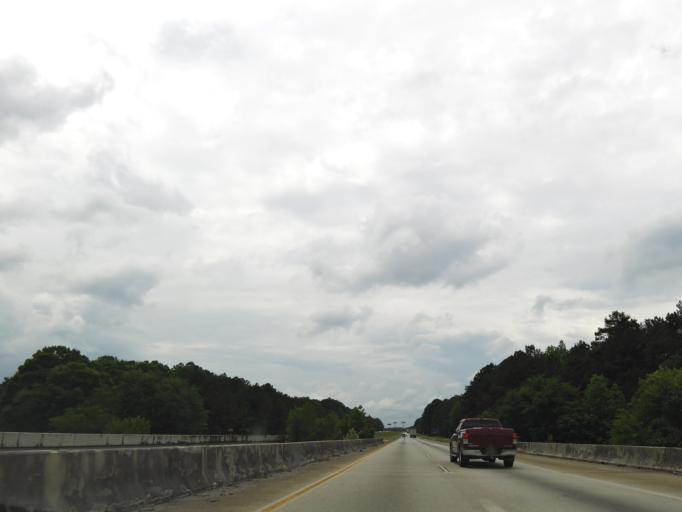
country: US
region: Georgia
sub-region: Carroll County
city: Temple
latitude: 33.7171
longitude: -84.9960
